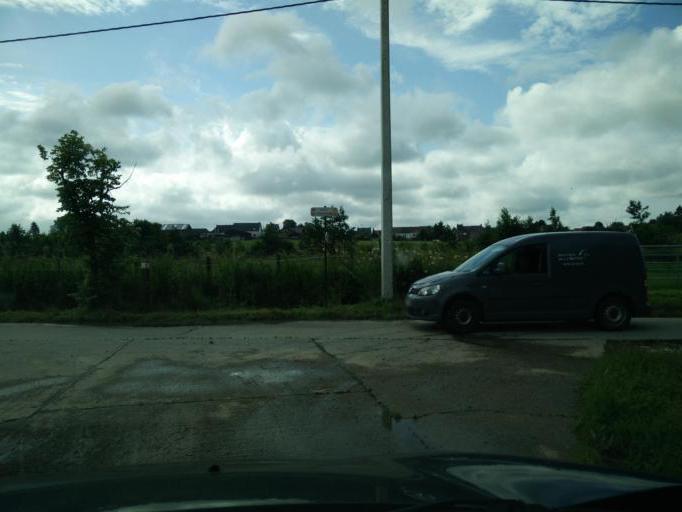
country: BE
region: Wallonia
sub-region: Province du Hainaut
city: Flobecq
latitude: 50.7988
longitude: 3.7506
